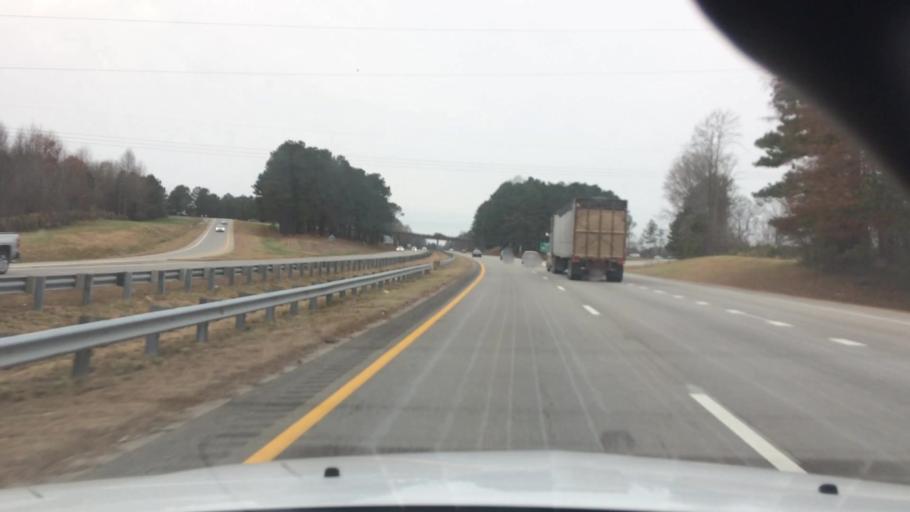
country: US
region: North Carolina
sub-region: Nash County
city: Red Oak
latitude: 35.9822
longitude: -77.8937
